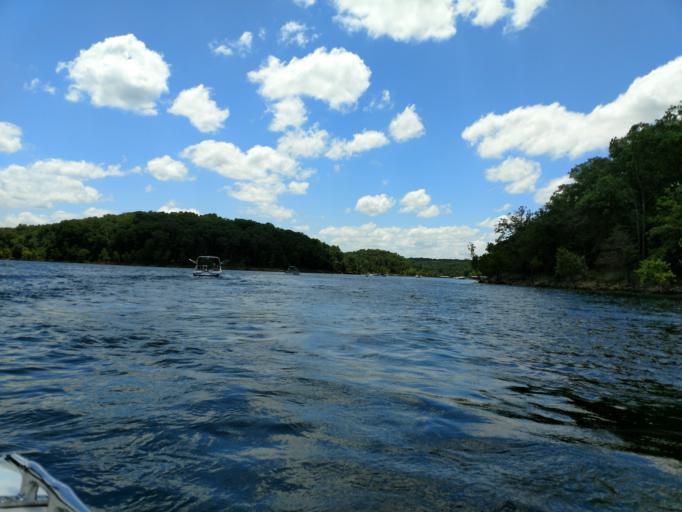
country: US
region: Missouri
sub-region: Barry County
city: Shell Knob
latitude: 36.5753
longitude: -93.5648
